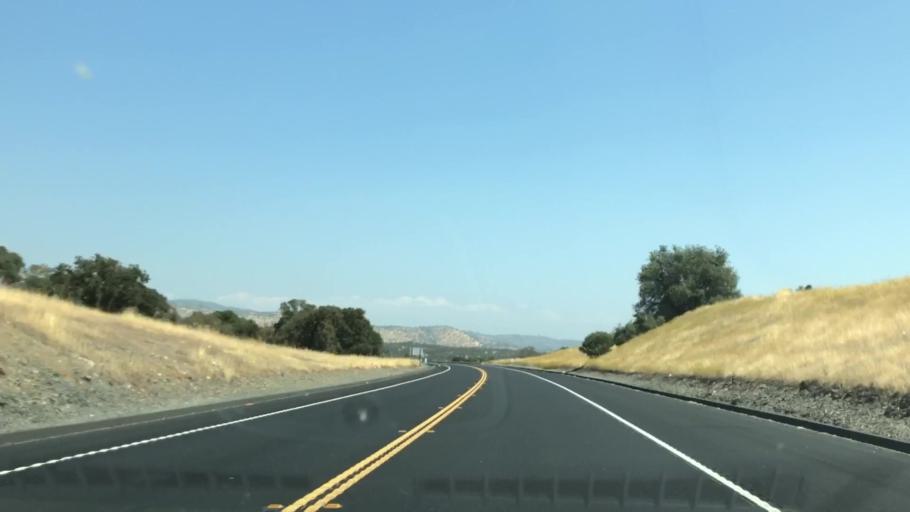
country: US
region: California
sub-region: Calaveras County
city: Copperopolis
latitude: 37.9564
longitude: -120.6813
